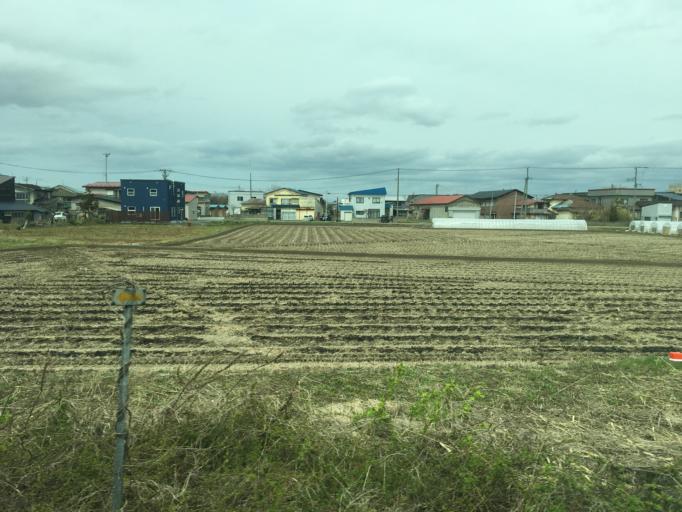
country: JP
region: Aomori
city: Shimokizukuri
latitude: 40.8031
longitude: 140.3902
